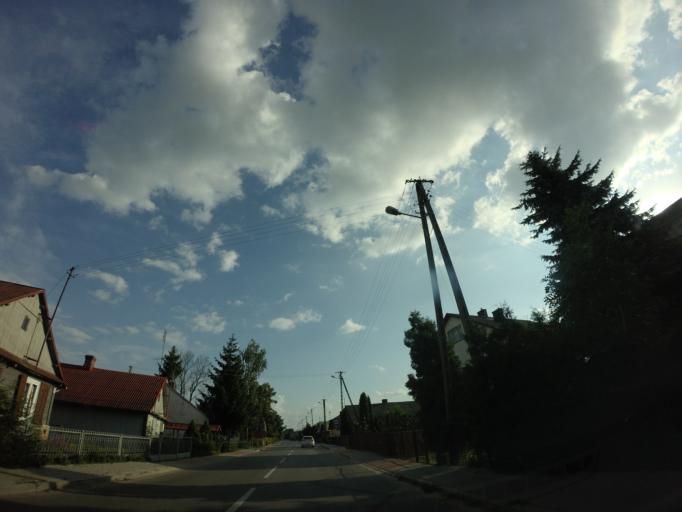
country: PL
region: Lublin Voivodeship
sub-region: Powiat lubartowski
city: Jeziorzany
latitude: 51.6045
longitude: 22.2775
